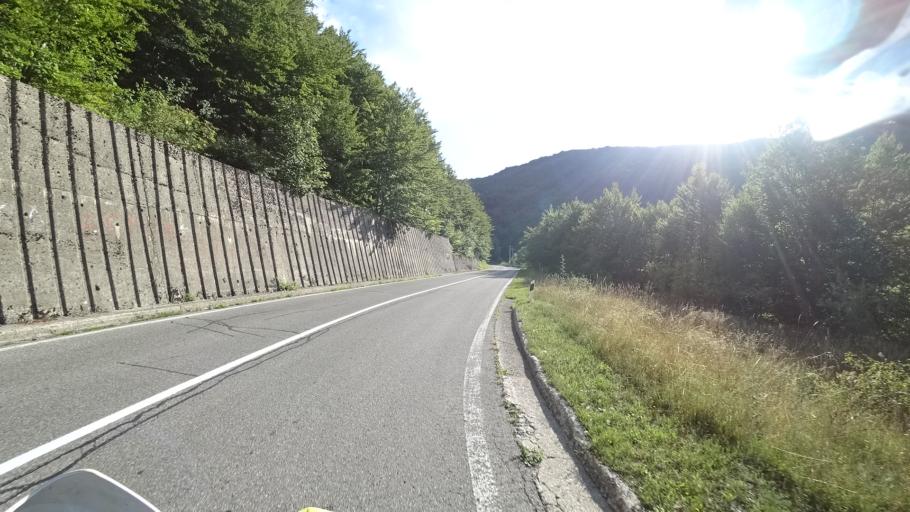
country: HR
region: Zadarska
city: Gracac
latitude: 44.2938
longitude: 16.0995
